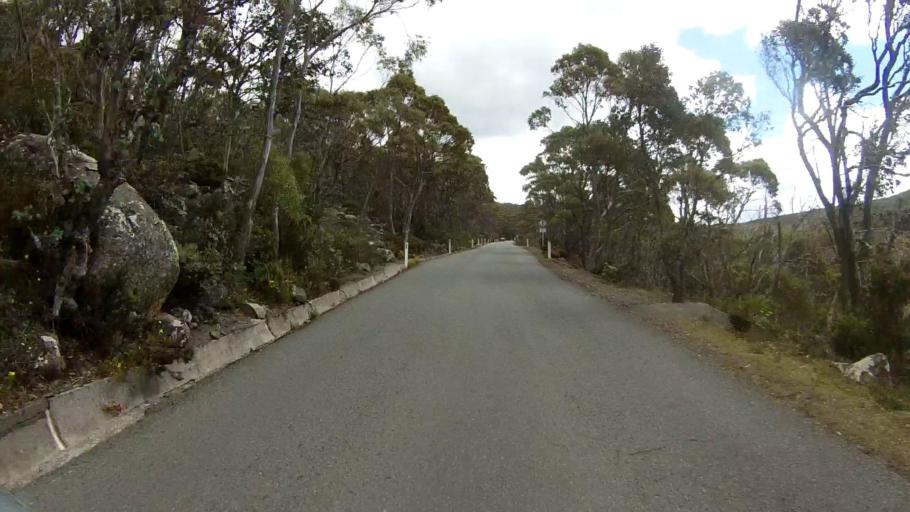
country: AU
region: Tasmania
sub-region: Glenorchy
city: West Moonah
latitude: -42.8878
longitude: 147.2277
